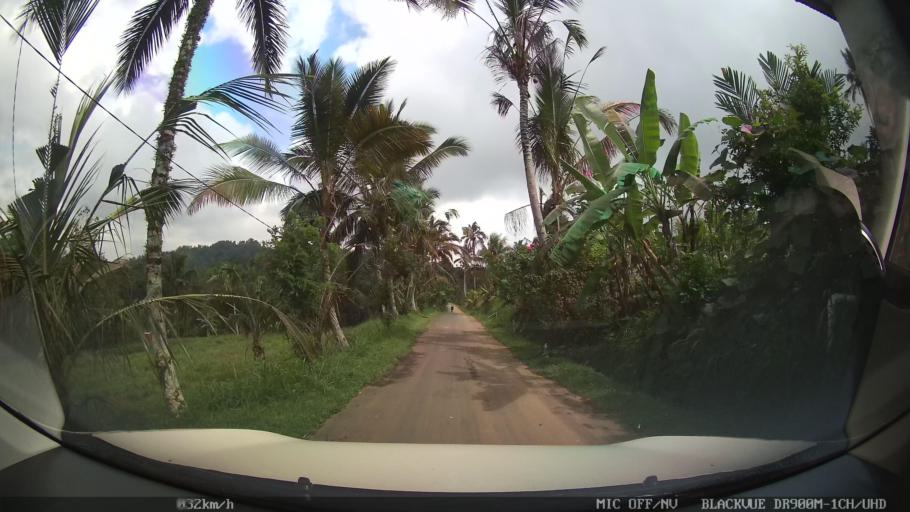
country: ID
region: Bali
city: Peneng
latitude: -8.3545
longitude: 115.2052
